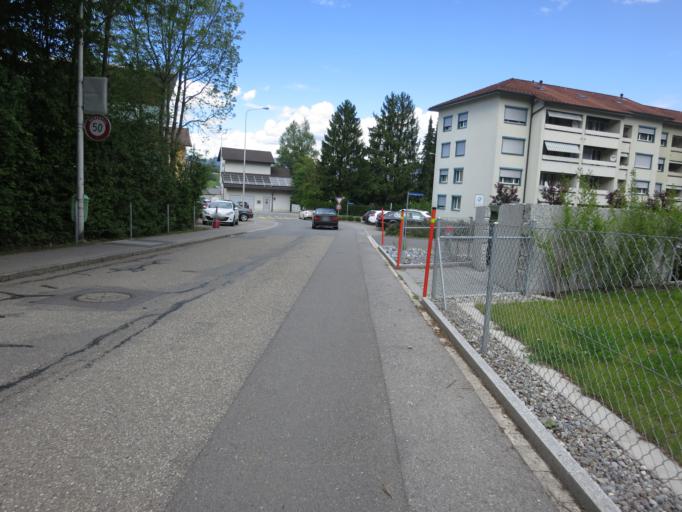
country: CH
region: Schwyz
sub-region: Bezirk March
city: Schubelbach
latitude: 47.1748
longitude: 8.9399
